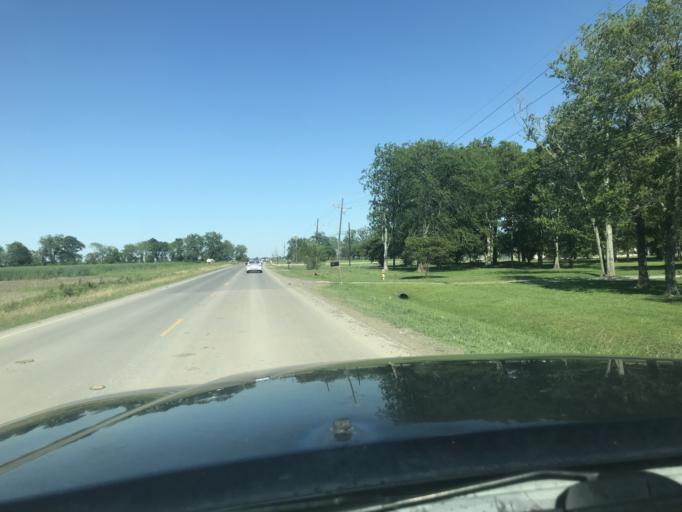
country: US
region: Louisiana
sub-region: West Baton Rouge Parish
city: Erwinville
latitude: 30.4688
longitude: -91.3264
